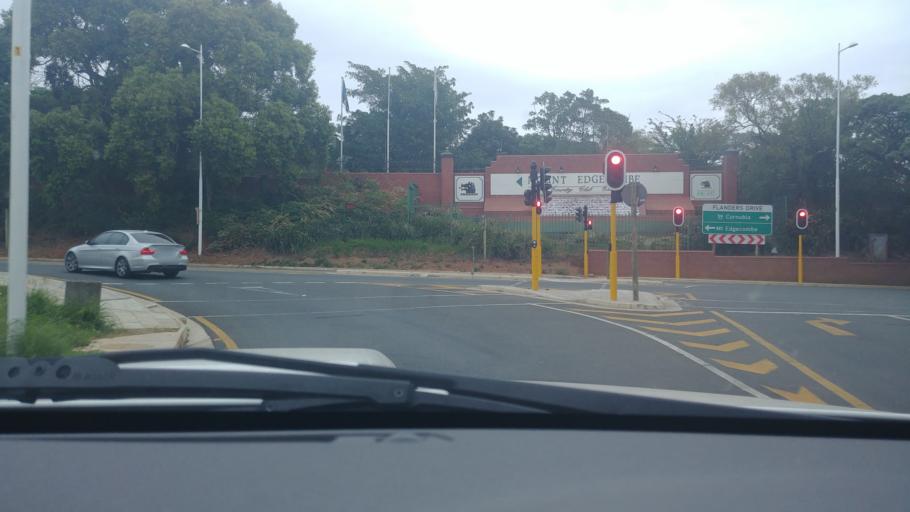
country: ZA
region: KwaZulu-Natal
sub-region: eThekwini Metropolitan Municipality
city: Durban
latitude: -29.7140
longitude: 31.0522
